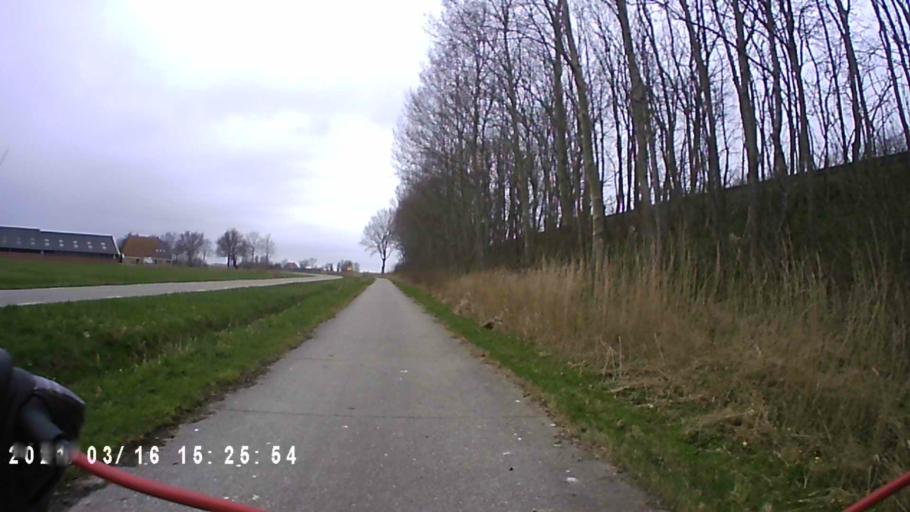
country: NL
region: Friesland
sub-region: Sudwest Fryslan
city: Bolsward
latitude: 53.0595
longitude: 5.5074
